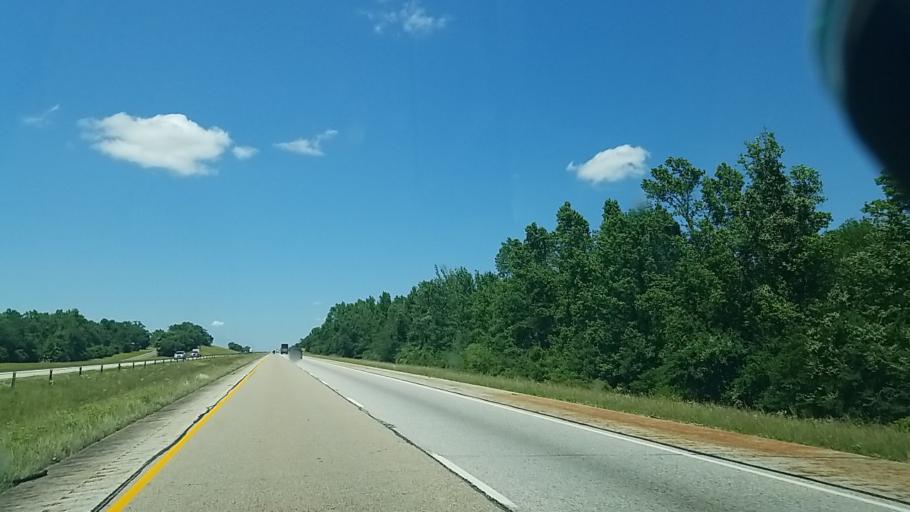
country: US
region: Texas
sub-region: Leon County
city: Centerville
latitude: 31.2155
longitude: -95.9964
